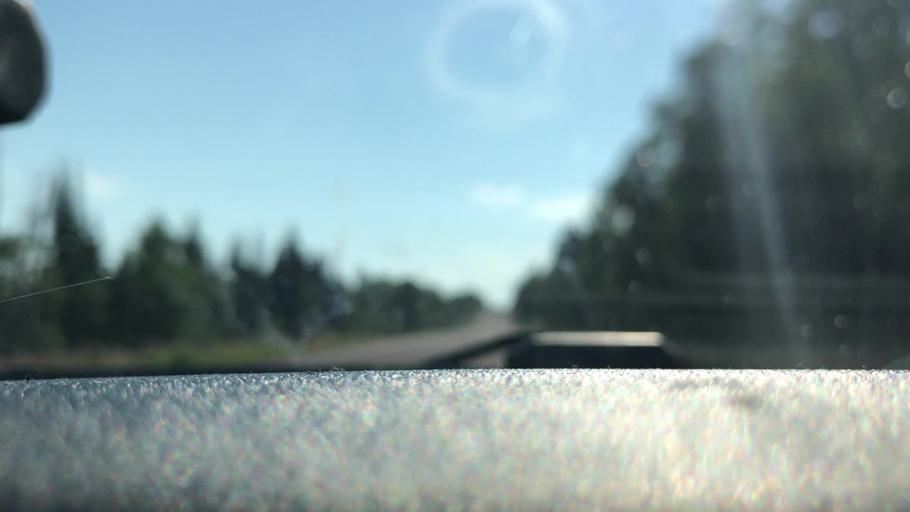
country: US
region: Minnesota
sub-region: Cook County
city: Grand Marais
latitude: 47.8308
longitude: -89.9818
